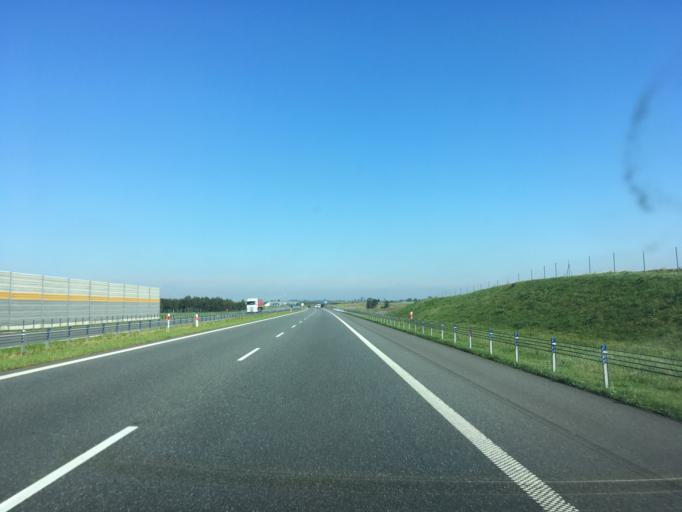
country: PL
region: Kujawsko-Pomorskie
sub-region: Powiat chelminski
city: Lisewo
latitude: 53.2461
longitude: 18.7259
